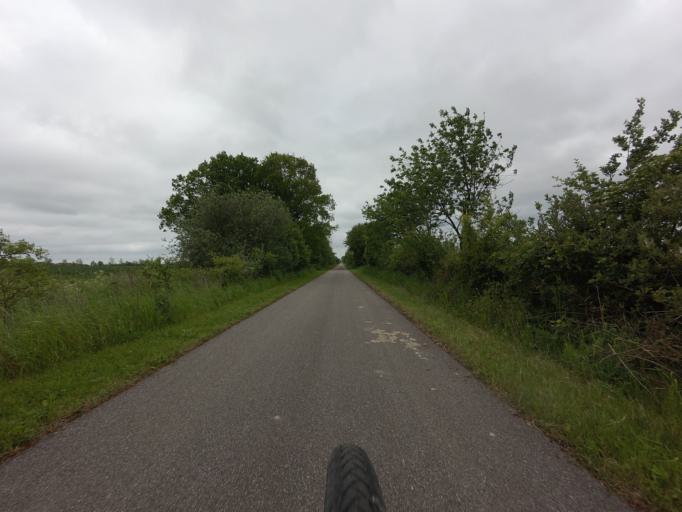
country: DK
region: Zealand
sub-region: Slagelse Kommune
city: Skaelskor
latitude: 55.2592
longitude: 11.3857
